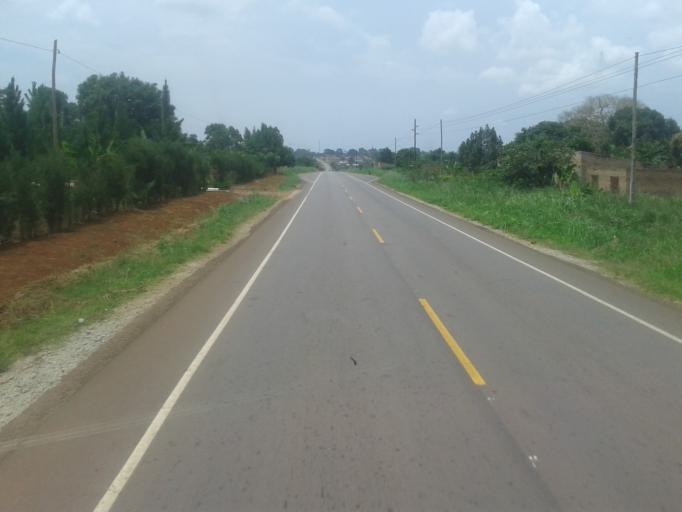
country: UG
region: Western Region
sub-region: Kiryandongo District
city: Kiryandongo
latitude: 1.8628
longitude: 32.0467
